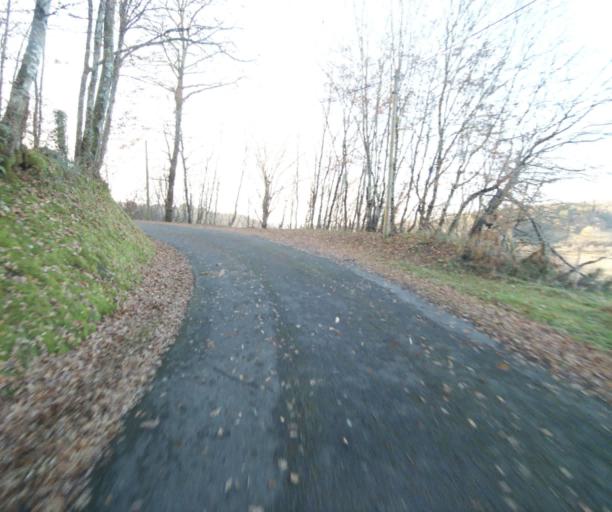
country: FR
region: Limousin
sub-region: Departement de la Correze
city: Laguenne
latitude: 45.2426
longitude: 1.8128
